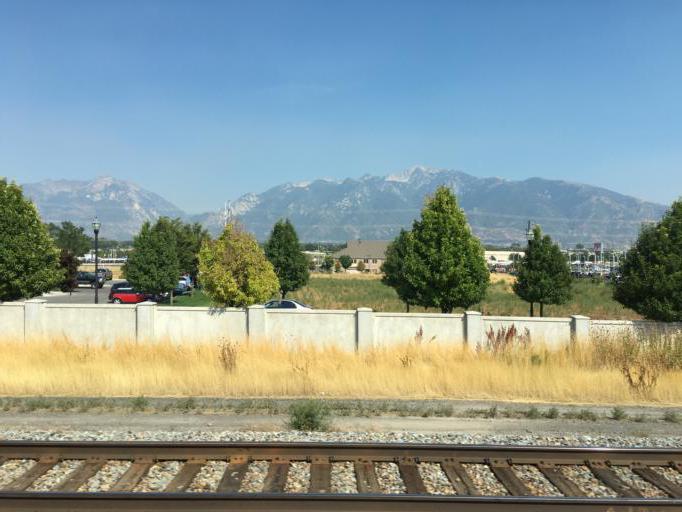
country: US
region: Utah
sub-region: Salt Lake County
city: South Jordan
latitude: 40.5523
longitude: -111.9020
